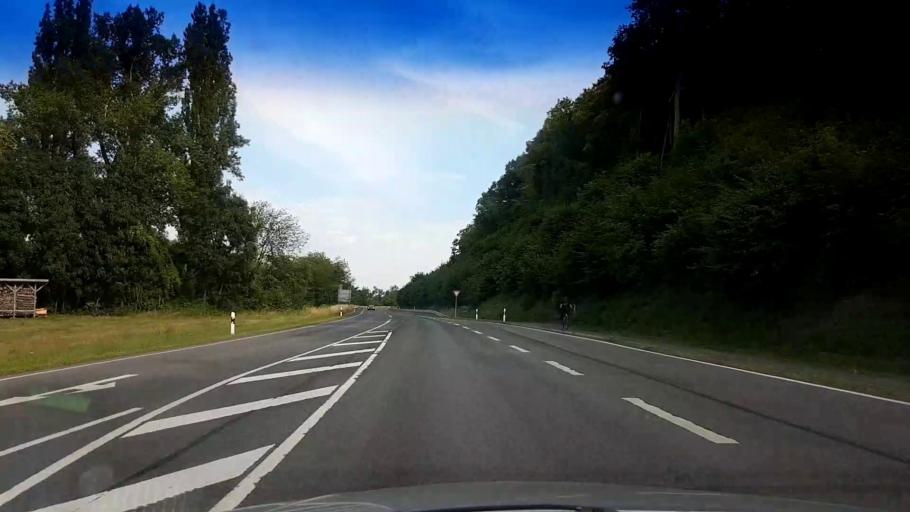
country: DE
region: Bavaria
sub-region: Regierungsbezirk Unterfranken
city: Stettfeld
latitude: 49.9654
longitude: 10.7037
